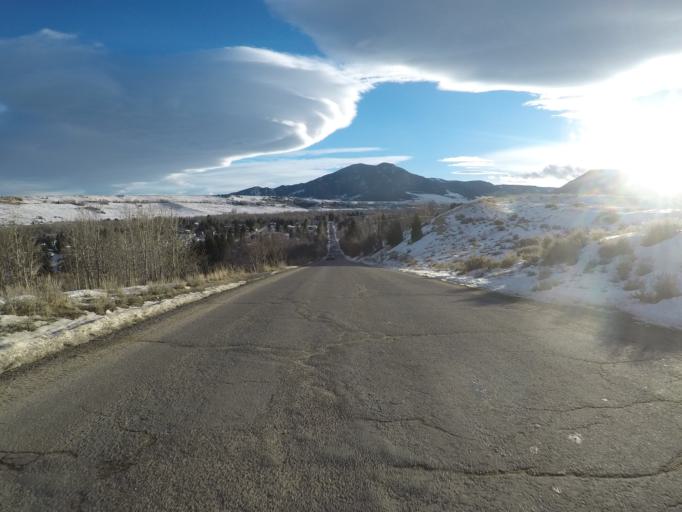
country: US
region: Montana
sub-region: Carbon County
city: Red Lodge
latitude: 45.1828
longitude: -109.2548
